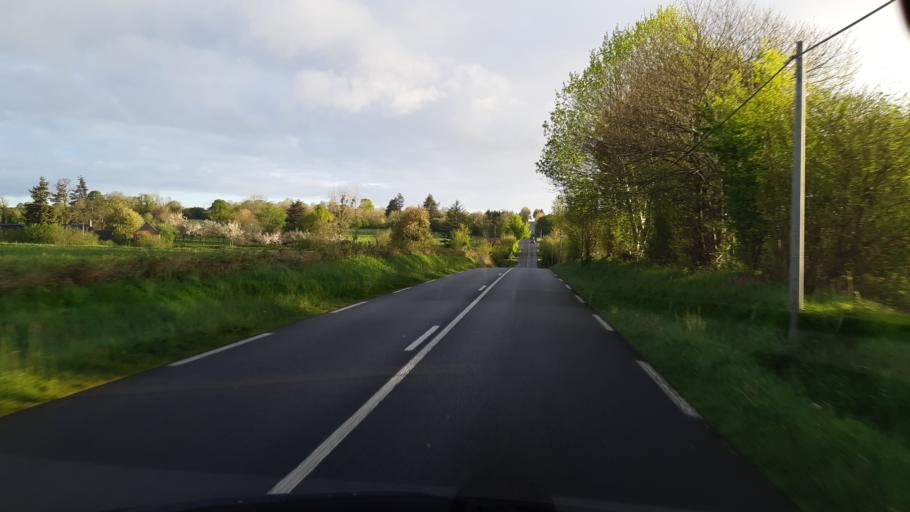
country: FR
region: Lower Normandy
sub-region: Departement de la Manche
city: Tessy-sur-Vire
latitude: 49.0195
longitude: -1.1473
